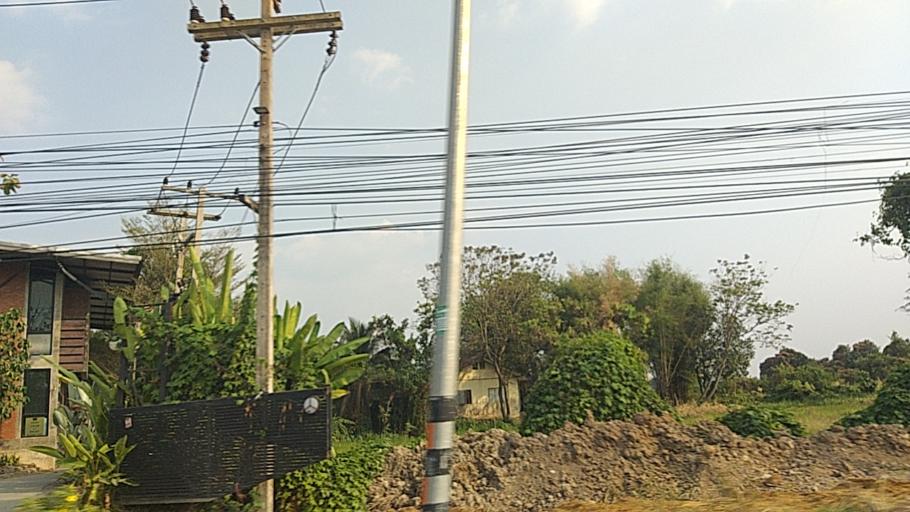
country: TH
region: Nakhon Nayok
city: Nakhon Nayok
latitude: 14.2534
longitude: 101.2592
